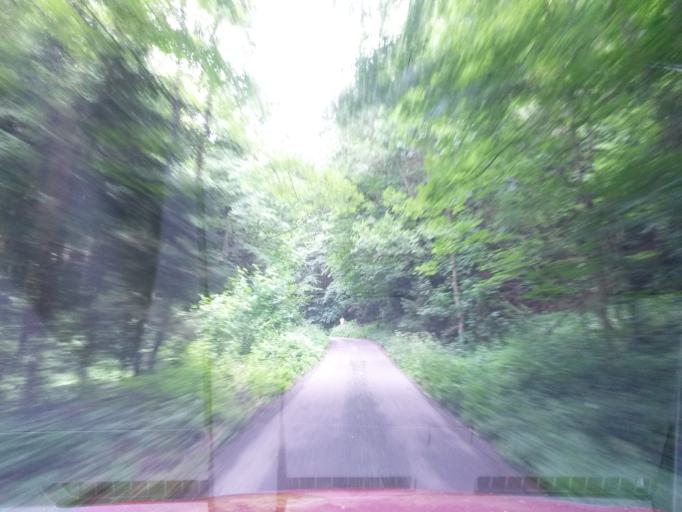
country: SK
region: Banskobystricky
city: Detva
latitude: 48.4834
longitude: 19.2909
